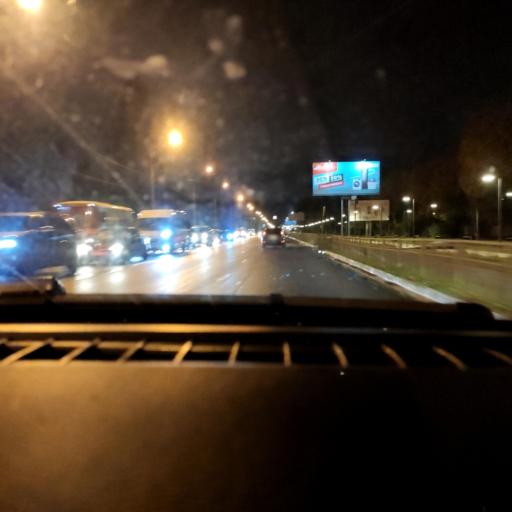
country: RU
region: Voronezj
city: Voronezh
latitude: 51.6667
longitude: 39.2655
